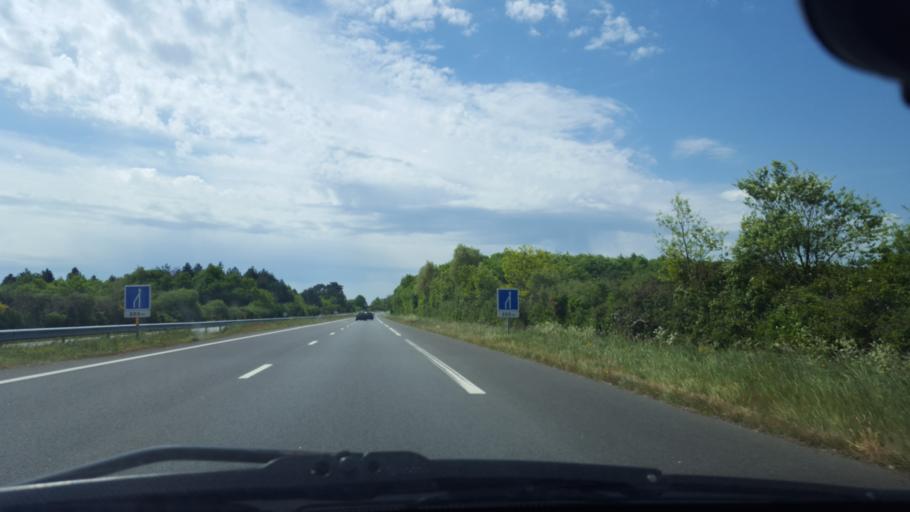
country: FR
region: Pays de la Loire
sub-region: Departement de la Loire-Atlantique
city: Paulx
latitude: 47.0026
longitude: -1.7257
